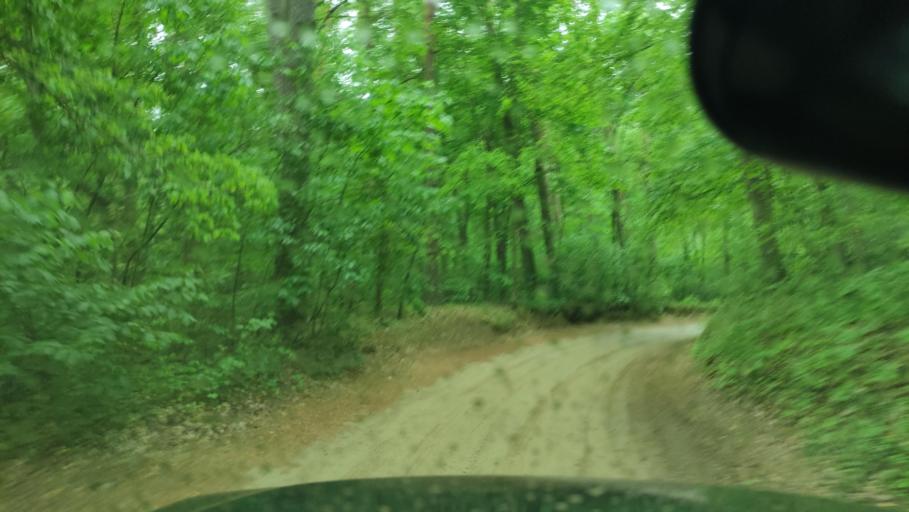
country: PL
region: Warmian-Masurian Voivodeship
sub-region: Powiat olsztynski
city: Olsztyn
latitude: 53.7602
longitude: 20.5222
